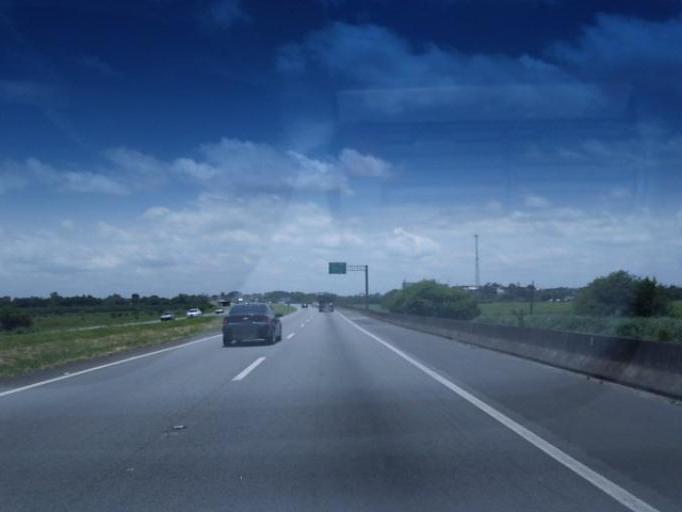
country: BR
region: Sao Paulo
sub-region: Registro
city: Registro
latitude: -24.4817
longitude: -47.8316
